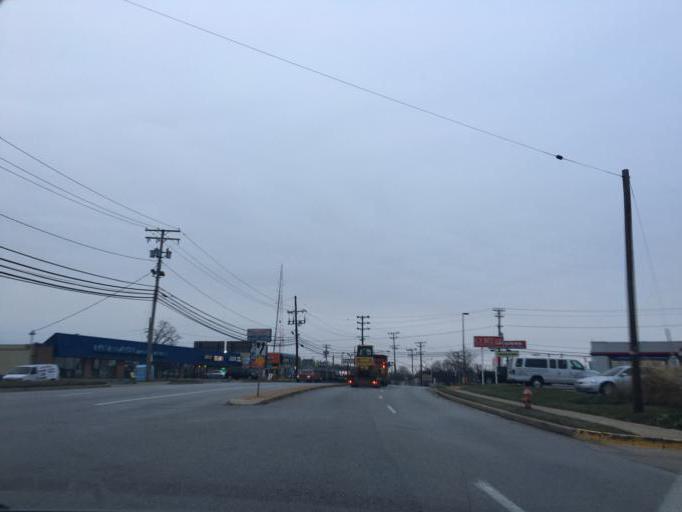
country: US
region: Maryland
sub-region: Baltimore County
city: Catonsville
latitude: 39.2862
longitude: -76.7529
